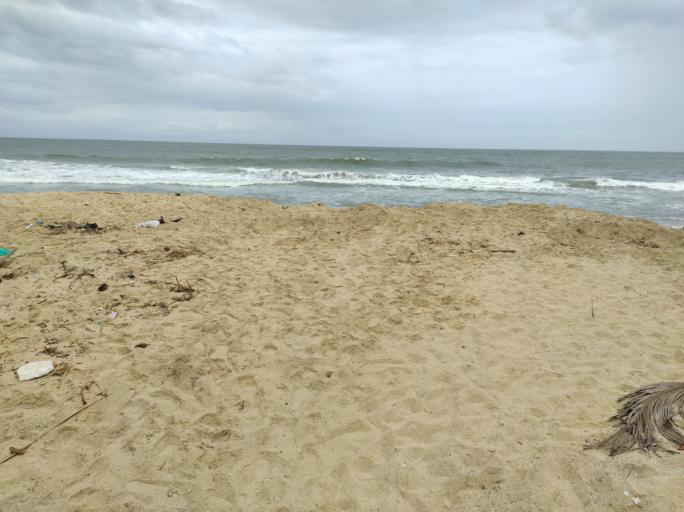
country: IN
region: Kerala
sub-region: Alappuzha
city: Vayalar
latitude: 9.7409
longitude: 76.2850
